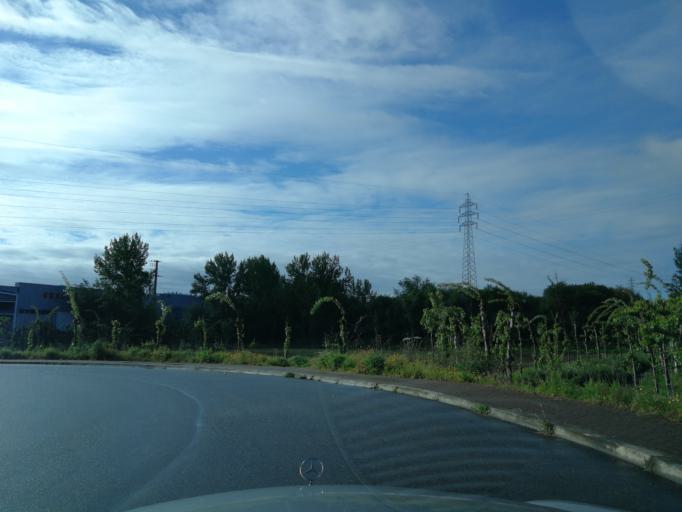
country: PT
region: Braga
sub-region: Braga
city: Braga
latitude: 41.5656
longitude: -8.4476
